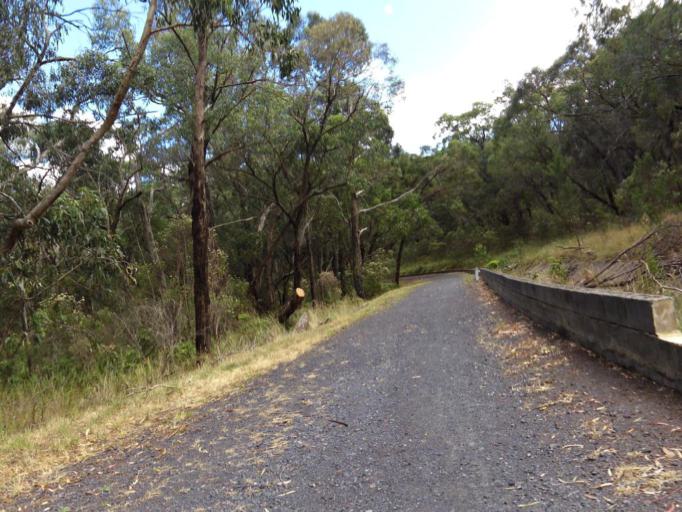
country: AU
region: Victoria
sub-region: Cardinia
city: Officer
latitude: -38.0376
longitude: 145.4521
